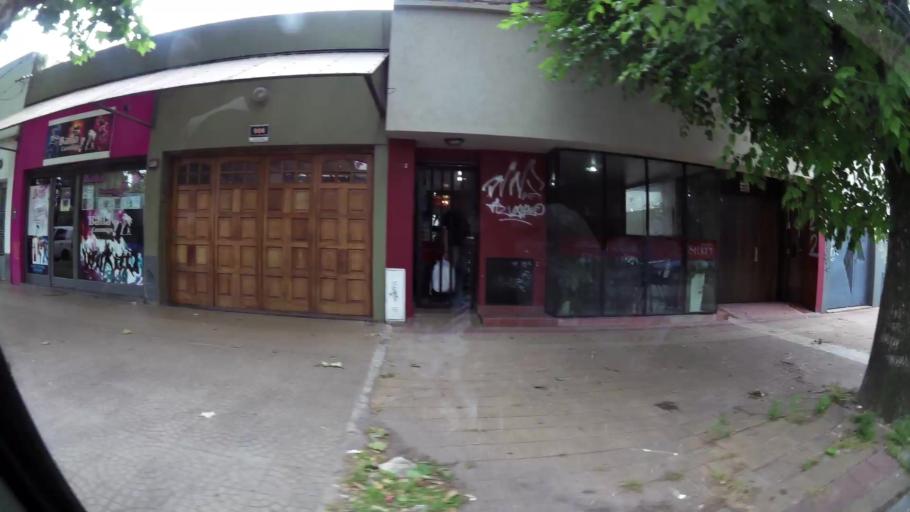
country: AR
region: Buenos Aires
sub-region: Partido de La Plata
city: La Plata
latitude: -34.9356
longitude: -57.9578
